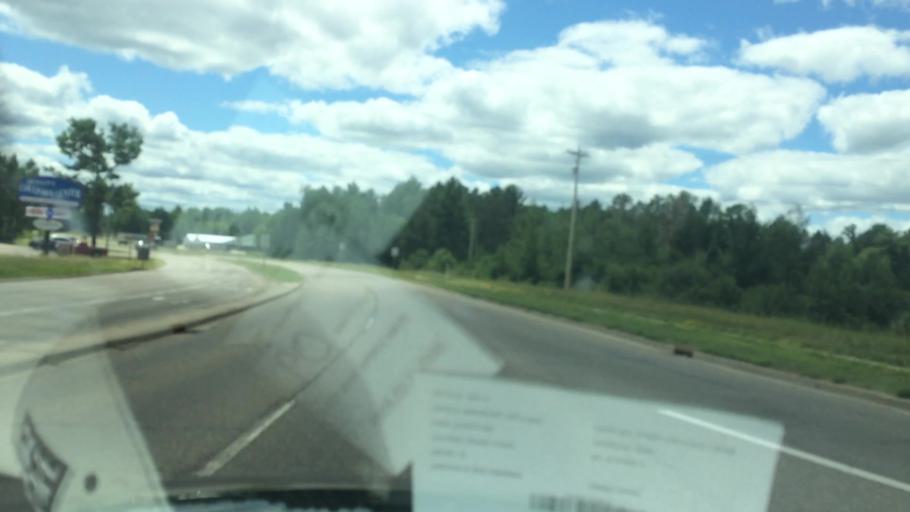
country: US
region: Wisconsin
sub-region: Oneida County
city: Rhinelander
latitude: 45.6562
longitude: -89.3808
